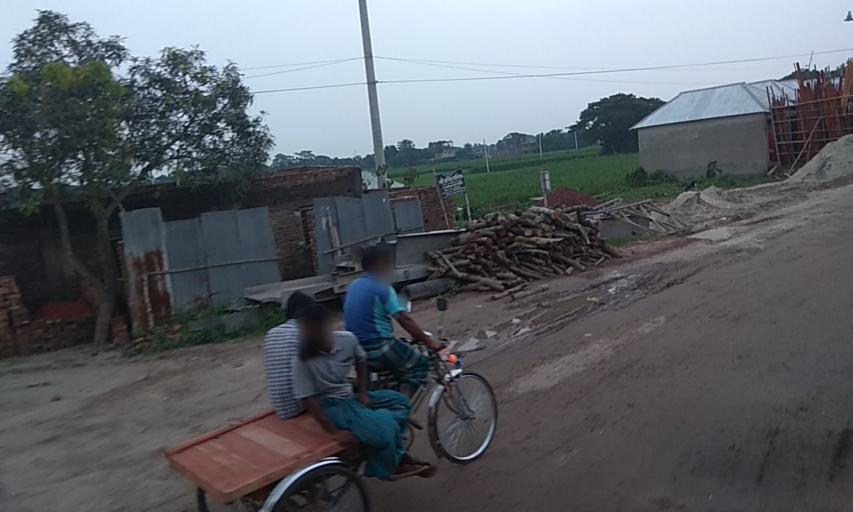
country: BD
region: Dhaka
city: Char Bhadrasan
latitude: 23.3730
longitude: 90.0296
